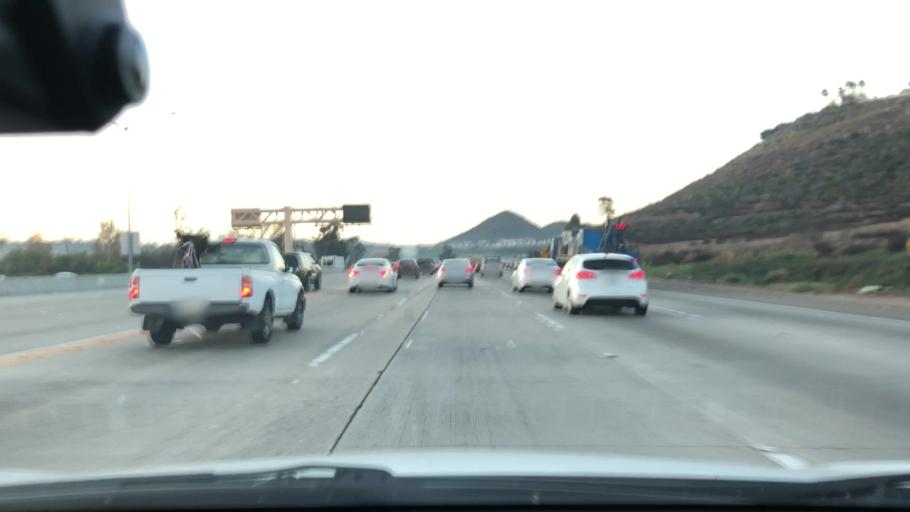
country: US
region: California
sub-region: San Diego County
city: Escondido
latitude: 33.0678
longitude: -117.0695
